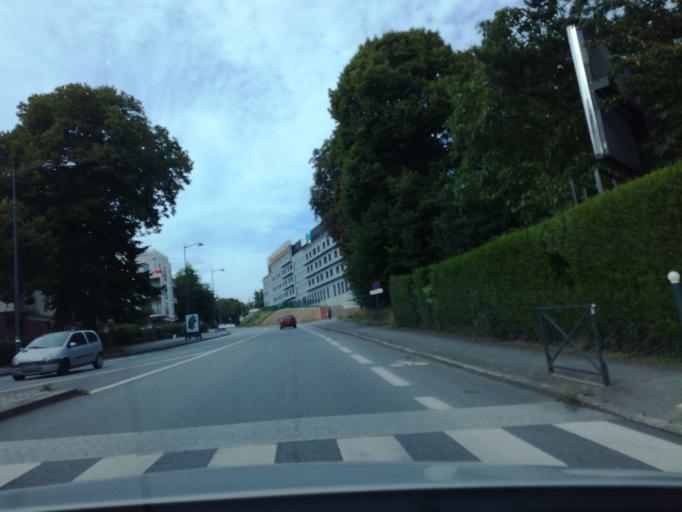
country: FR
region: Brittany
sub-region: Departement d'Ille-et-Vilaine
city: Rennes
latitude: 48.1366
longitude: -1.6590
